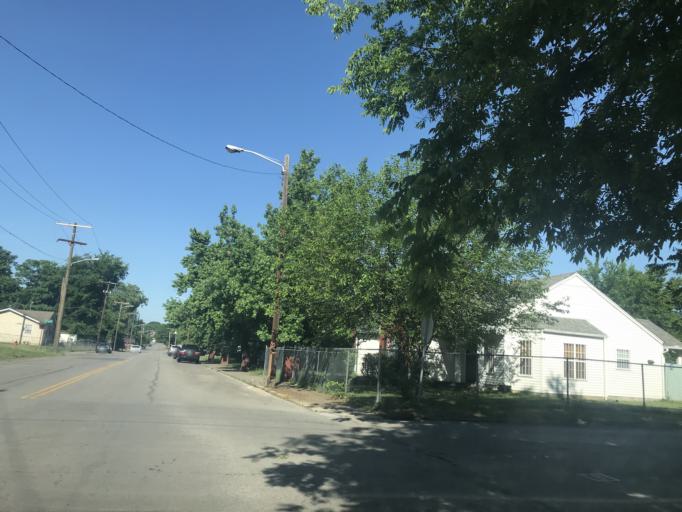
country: US
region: Tennessee
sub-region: Davidson County
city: Nashville
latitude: 36.1844
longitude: -86.8053
